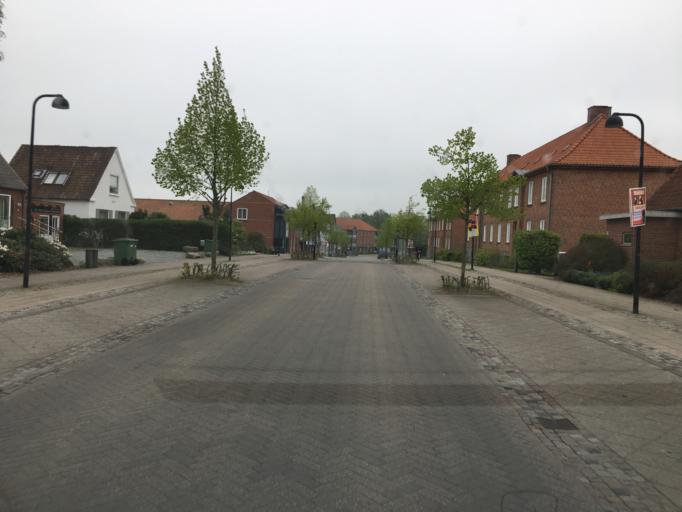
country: DK
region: South Denmark
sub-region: Aabenraa Kommune
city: Padborg
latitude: 54.8223
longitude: 9.3619
